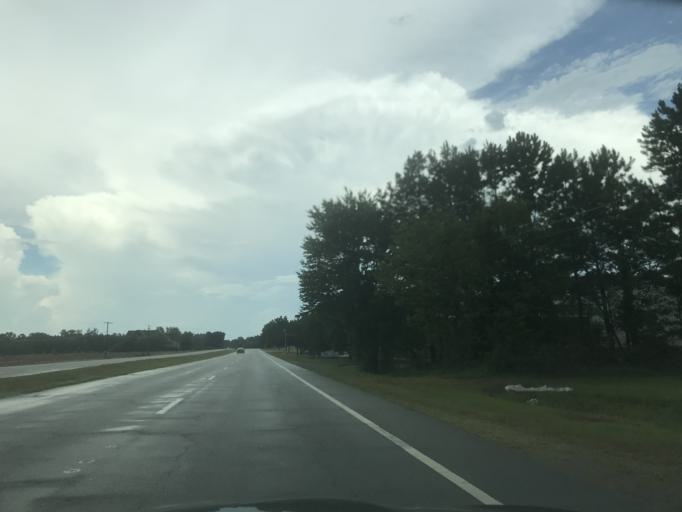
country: US
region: North Carolina
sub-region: Johnston County
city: Wilsons Mills
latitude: 35.5628
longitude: -78.3914
